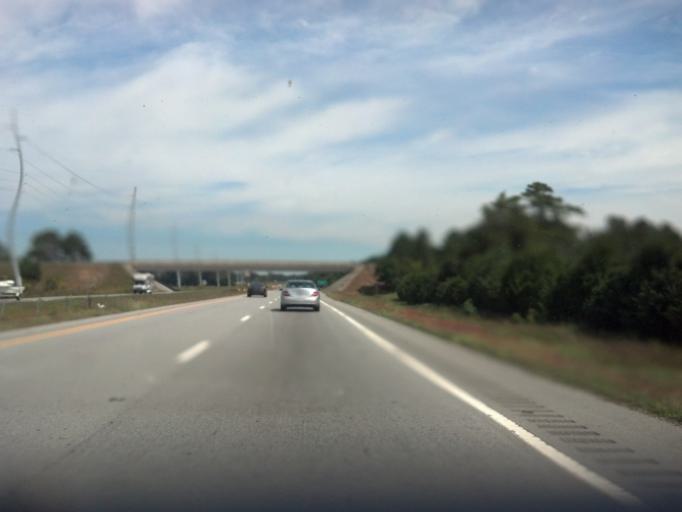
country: US
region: North Carolina
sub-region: Pitt County
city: Greenville
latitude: 35.6491
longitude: -77.4197
